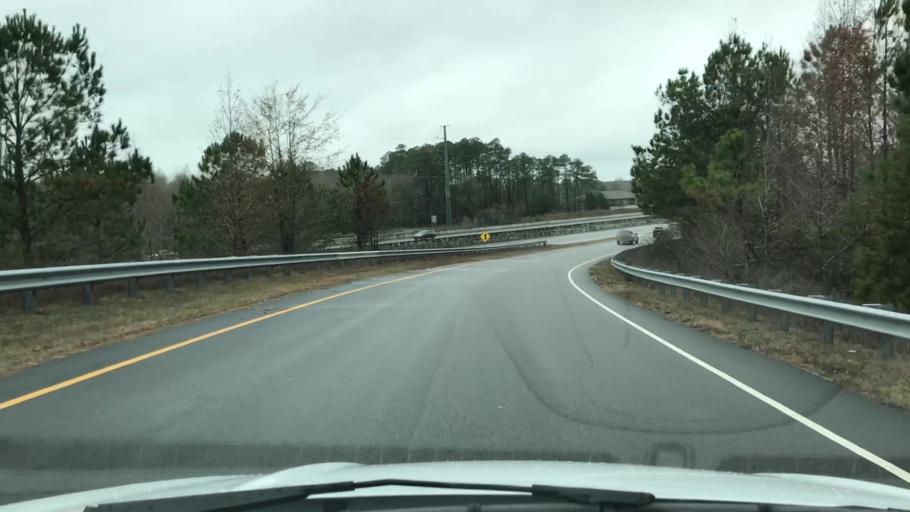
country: US
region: South Carolina
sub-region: Horry County
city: Forestbrook
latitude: 33.7421
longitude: -78.9521
